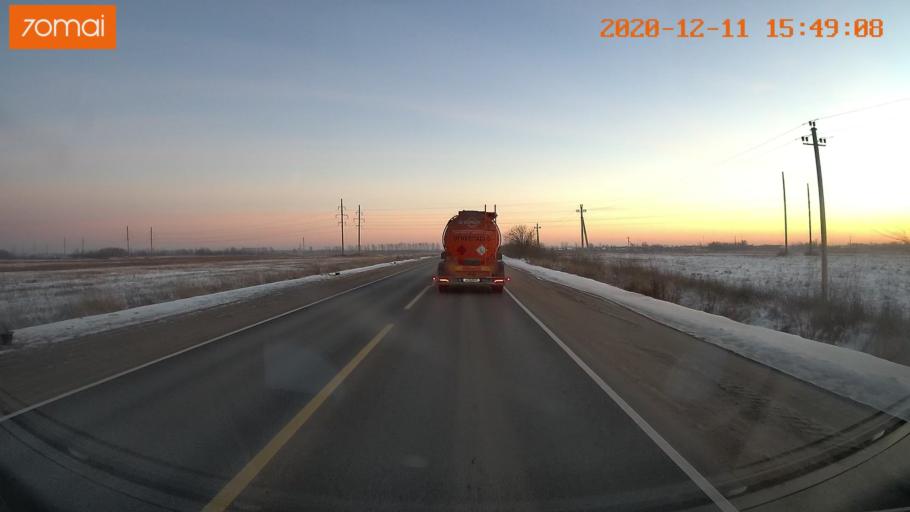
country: RU
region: Ivanovo
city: Novo-Talitsy
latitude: 56.9899
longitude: 40.8722
